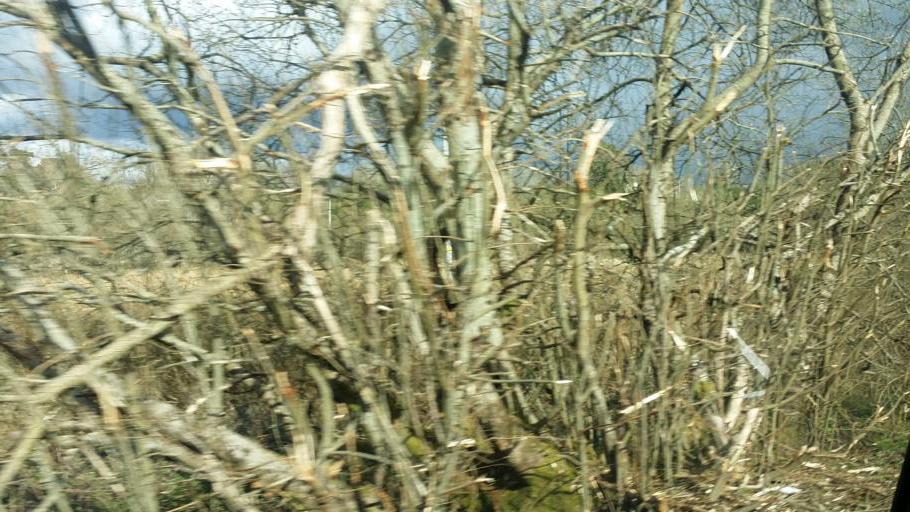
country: IE
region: Connaught
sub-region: County Leitrim
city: Manorhamilton
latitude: 54.3123
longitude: -8.1873
